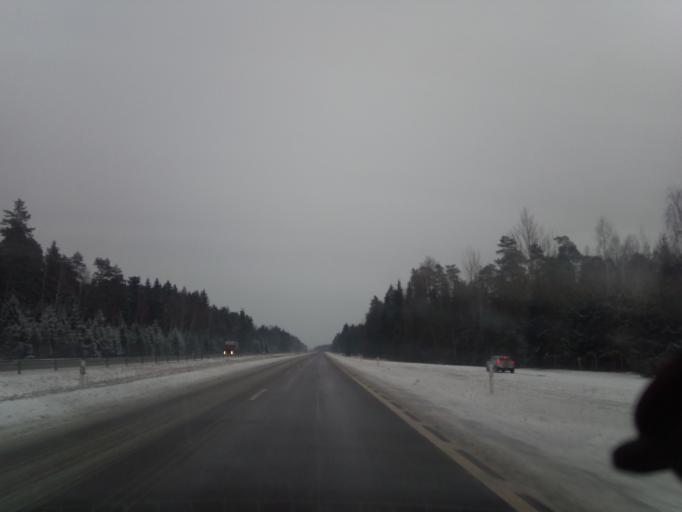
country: LT
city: Sirvintos
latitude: 54.9719
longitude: 24.9467
